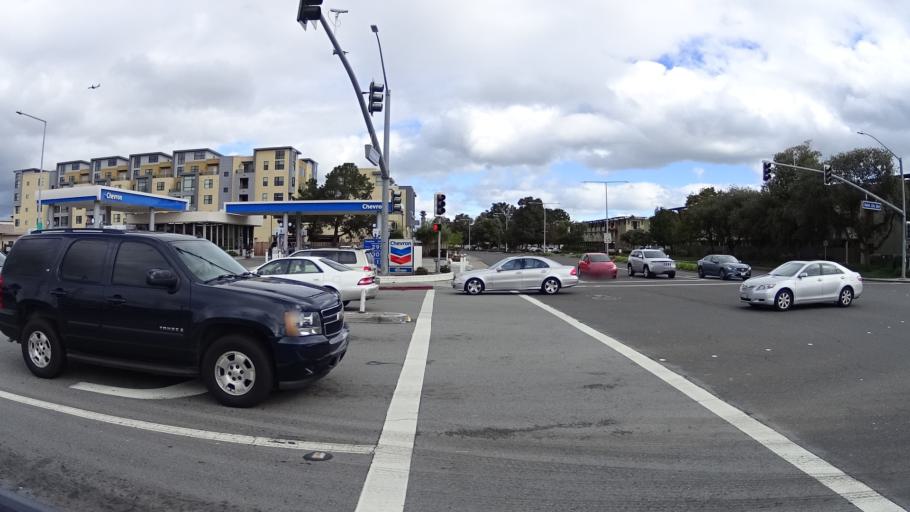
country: US
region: California
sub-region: San Mateo County
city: Foster City
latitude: 37.5614
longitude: -122.2693
